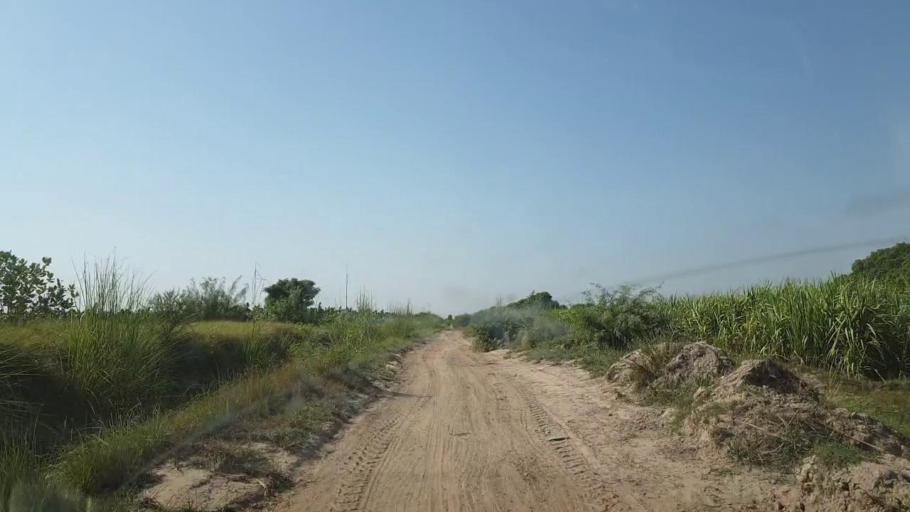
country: PK
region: Sindh
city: Tando Jam
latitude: 25.3175
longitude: 68.6036
